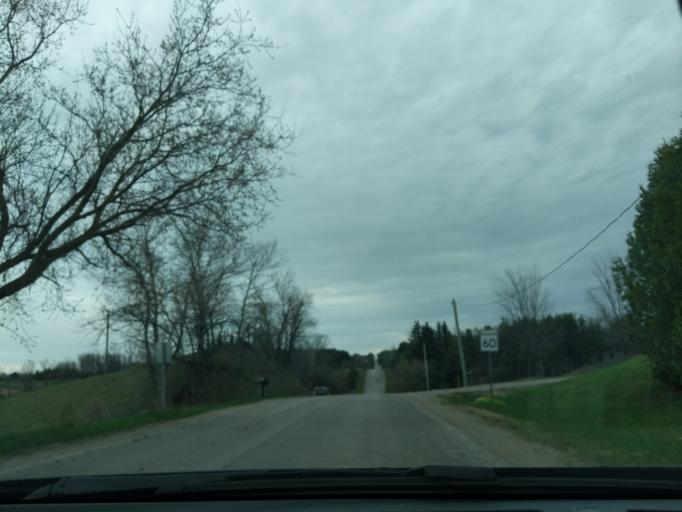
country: CA
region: Ontario
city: Orangeville
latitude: 44.0095
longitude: -79.9660
